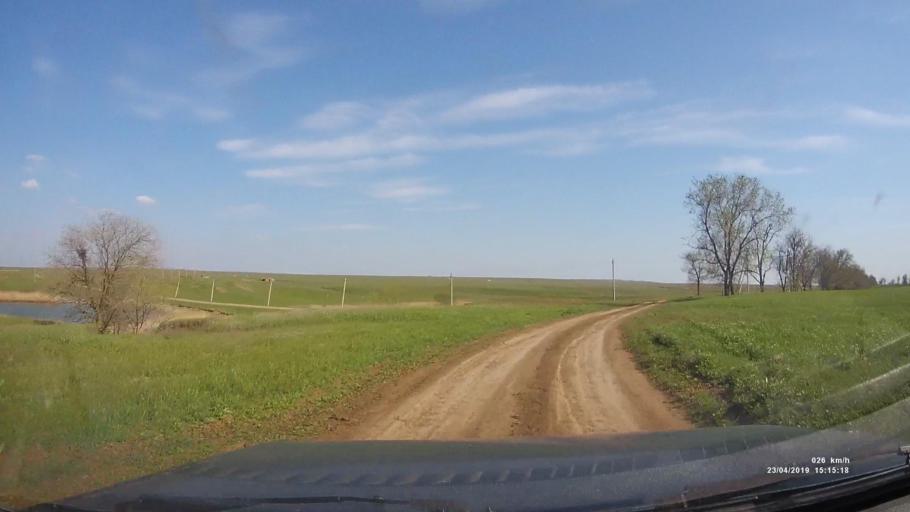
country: RU
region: Rostov
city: Remontnoye
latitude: 46.5395
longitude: 42.9691
